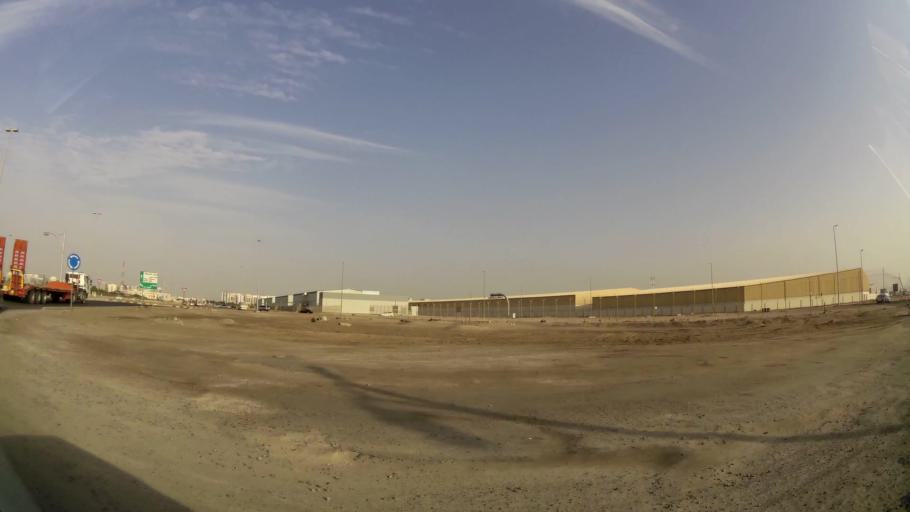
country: AE
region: Abu Dhabi
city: Abu Dhabi
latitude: 24.3372
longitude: 54.5163
